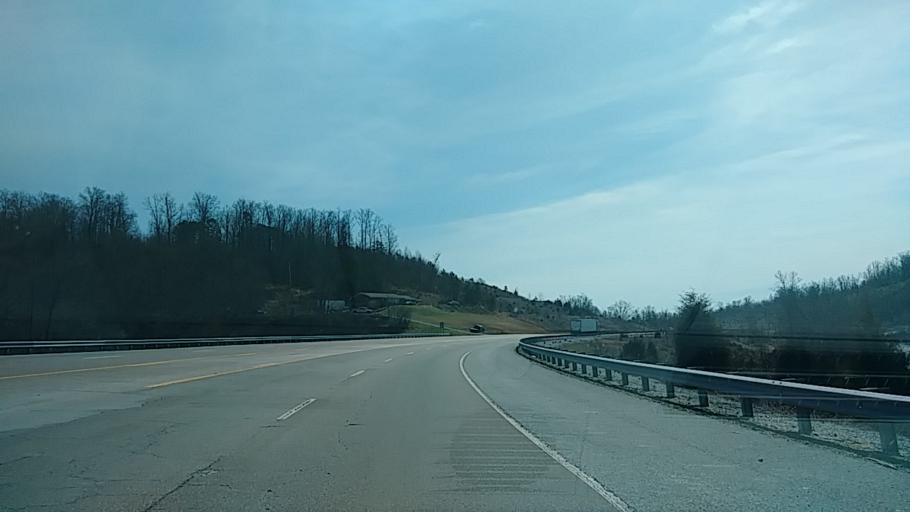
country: US
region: Tennessee
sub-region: Claiborne County
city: Tazewell
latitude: 36.4339
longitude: -83.5577
